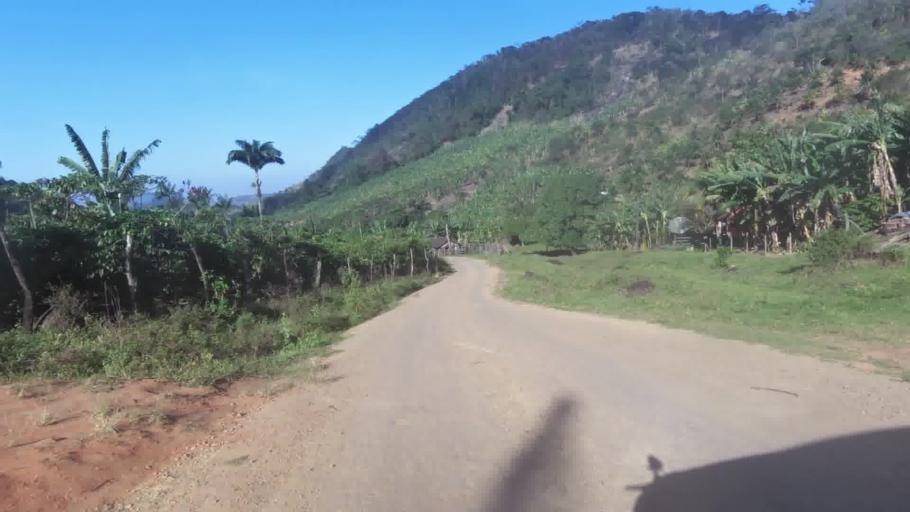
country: BR
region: Espirito Santo
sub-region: Iconha
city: Iconha
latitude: -20.7504
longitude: -40.8024
